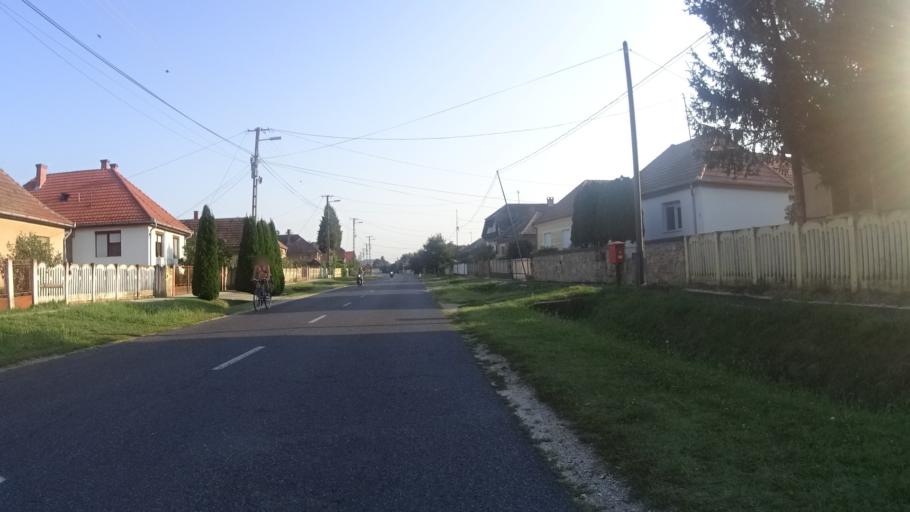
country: HU
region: Zala
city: Zalakomar
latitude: 46.6019
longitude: 17.1778
